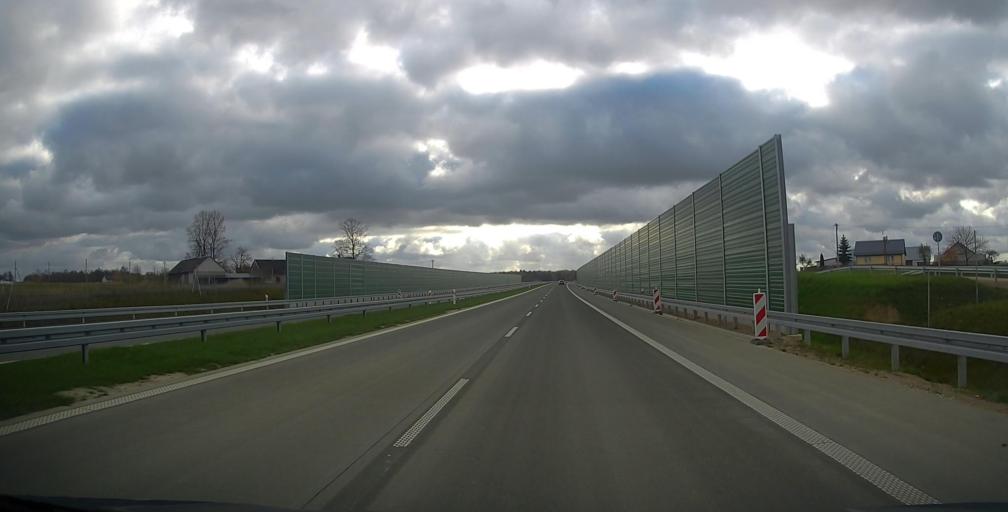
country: PL
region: Podlasie
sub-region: Powiat suwalski
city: Raczki
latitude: 53.9412
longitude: 22.7629
